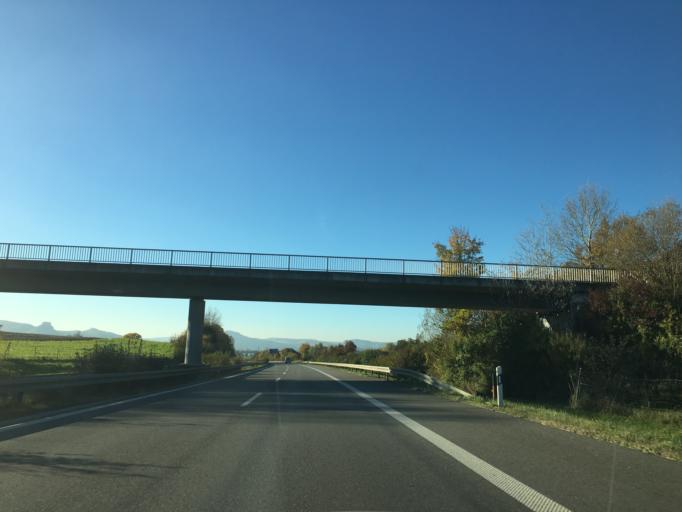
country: DE
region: Baden-Wuerttemberg
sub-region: Freiburg Region
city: Volkertshausen
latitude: 47.7907
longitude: 8.8846
